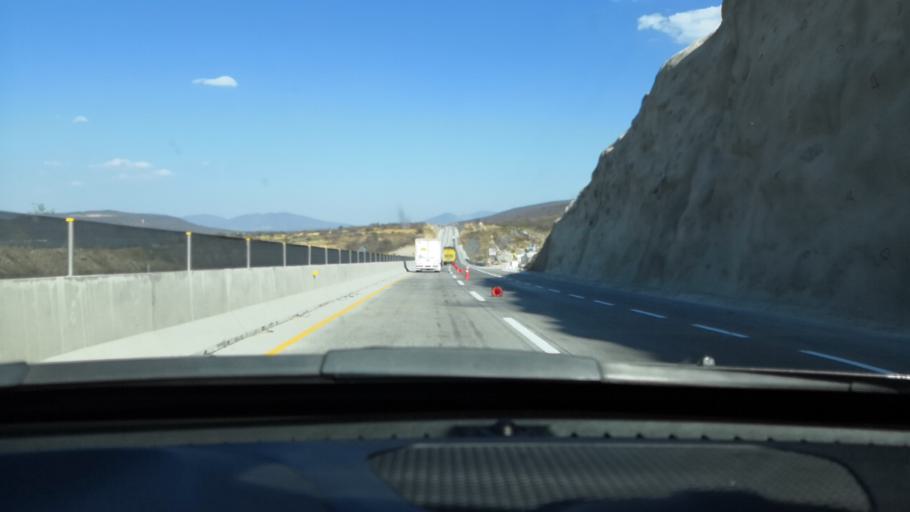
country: MX
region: Jalisco
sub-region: Tlajomulco de Zuniga
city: San Lucas Evangelista
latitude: 20.3917
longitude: -103.3311
